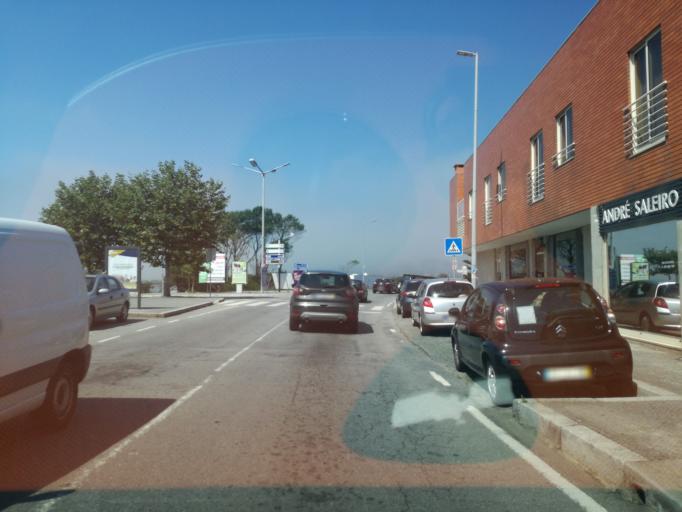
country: PT
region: Braga
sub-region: Esposende
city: Esposende
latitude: 41.5134
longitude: -8.7735
